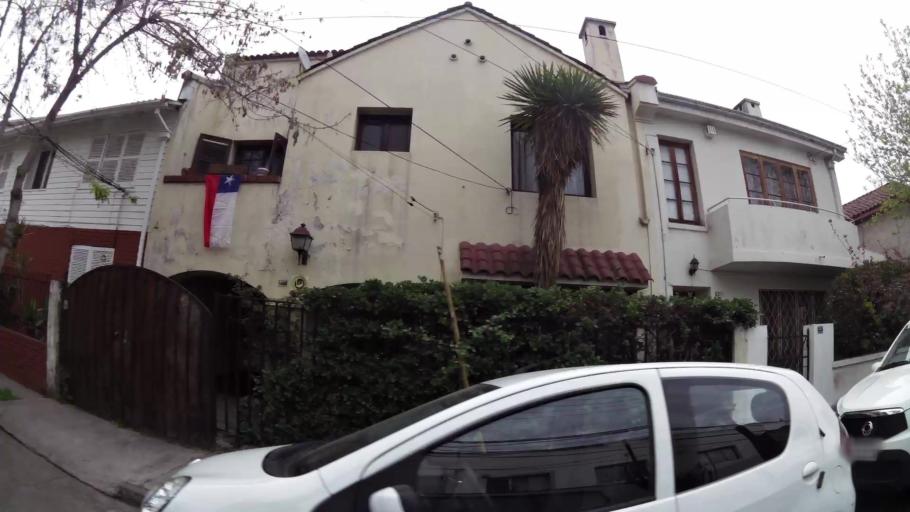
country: CL
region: Santiago Metropolitan
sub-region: Provincia de Santiago
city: Santiago
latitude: -33.4498
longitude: -70.6156
